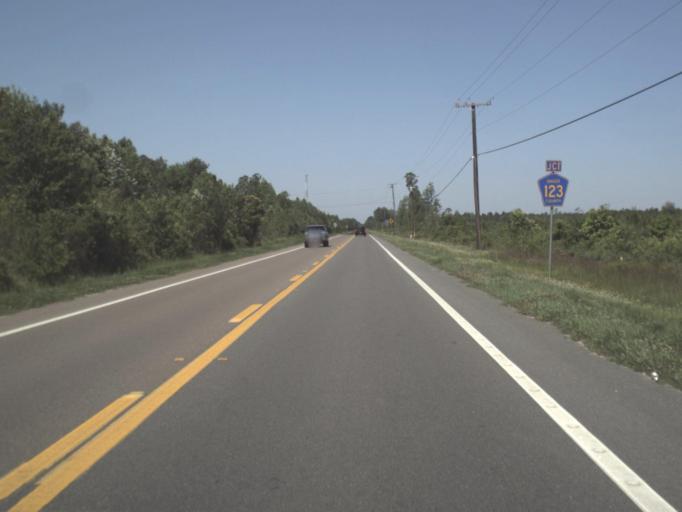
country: US
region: Florida
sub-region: Baker County
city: Macclenny
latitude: 30.2707
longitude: -82.1887
